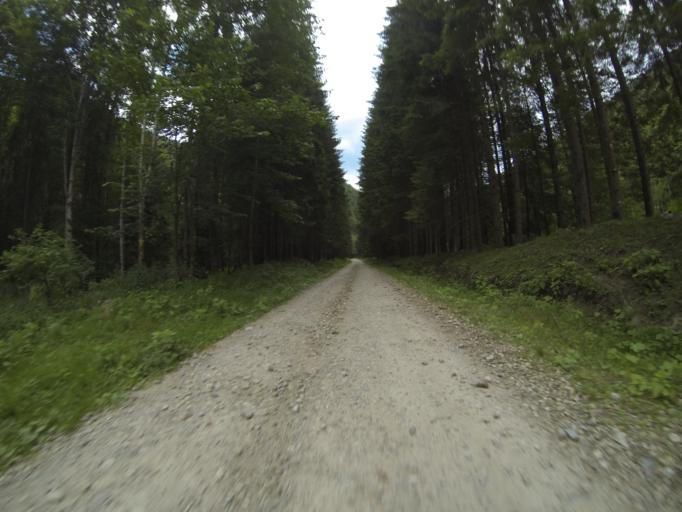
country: RO
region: Gorj
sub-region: Comuna Polovragi
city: Polovragi
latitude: 45.2631
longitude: 23.7710
